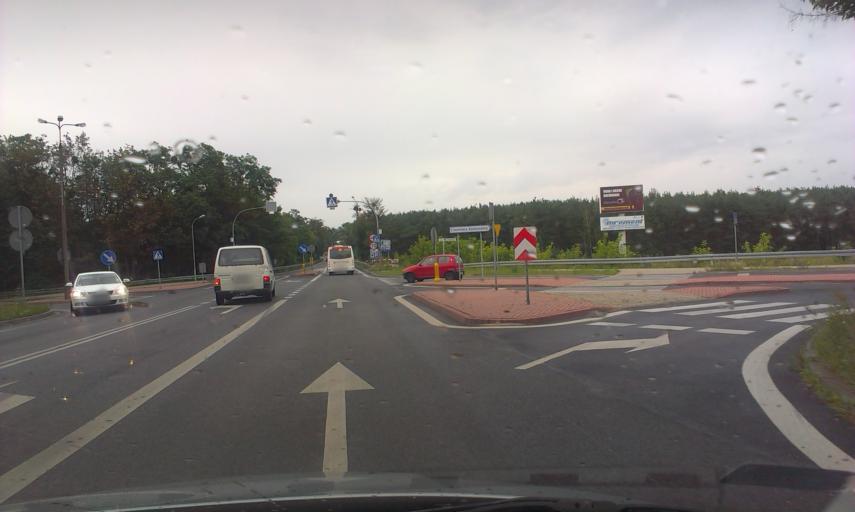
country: PL
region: Greater Poland Voivodeship
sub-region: Powiat obornicki
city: Oborniki
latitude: 52.6329
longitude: 16.8108
